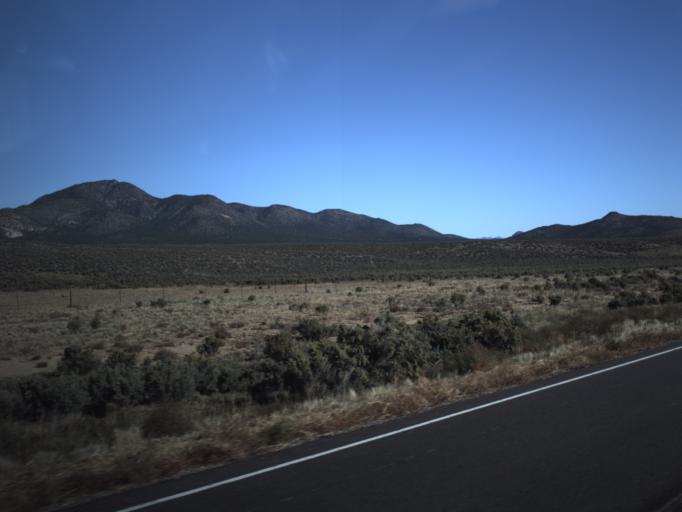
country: US
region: Utah
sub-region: Washington County
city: Enterprise
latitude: 37.7741
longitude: -113.9736
